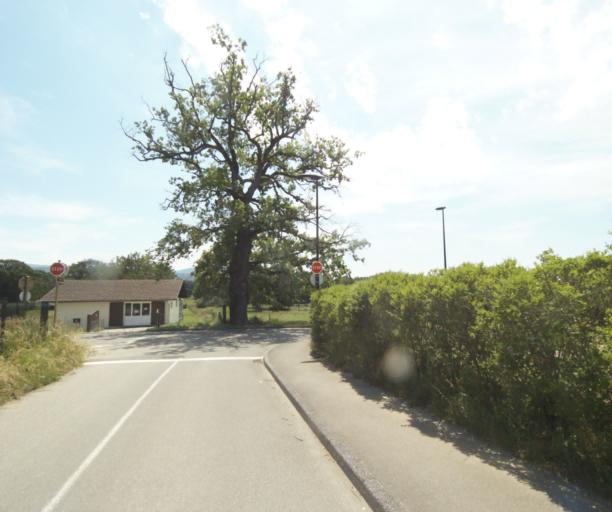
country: FR
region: Rhone-Alpes
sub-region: Departement de la Haute-Savoie
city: Messery
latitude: 46.3519
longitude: 6.3199
